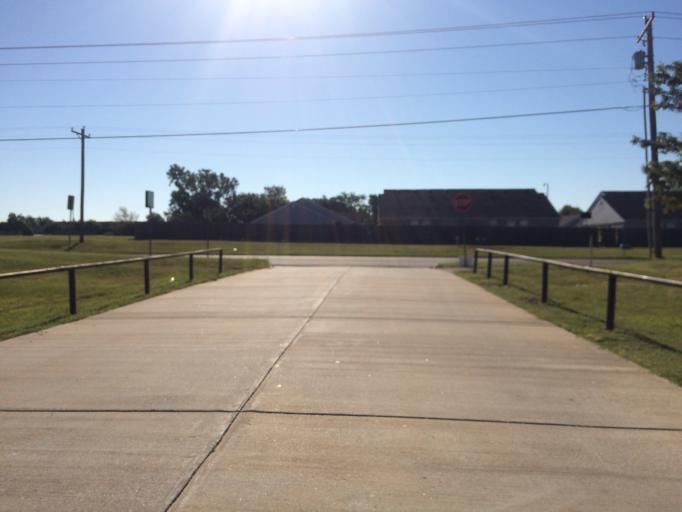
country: US
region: Oklahoma
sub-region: Cleveland County
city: Hall Park
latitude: 35.2383
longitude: -97.4240
